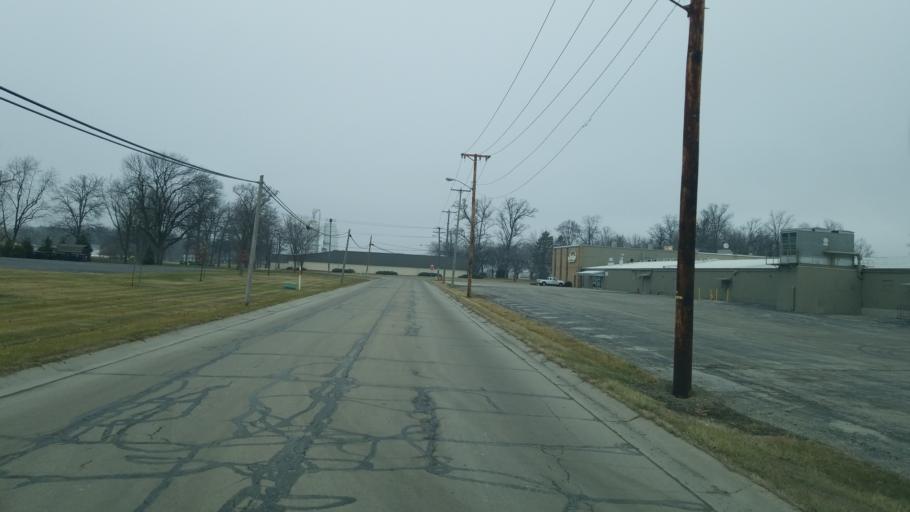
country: US
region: Indiana
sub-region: Adams County
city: Berne
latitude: 40.6639
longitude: -84.9470
